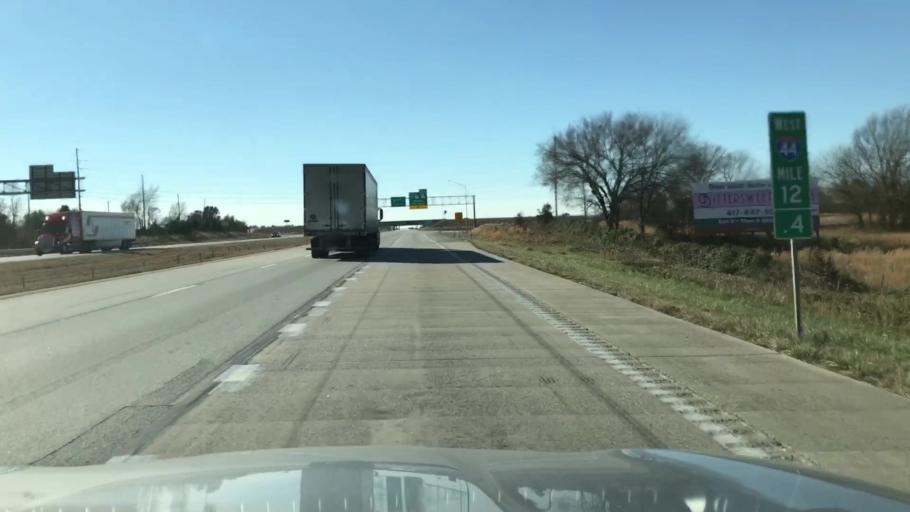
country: US
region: Missouri
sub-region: Jasper County
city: Duenweg
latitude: 37.0645
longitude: -94.4187
